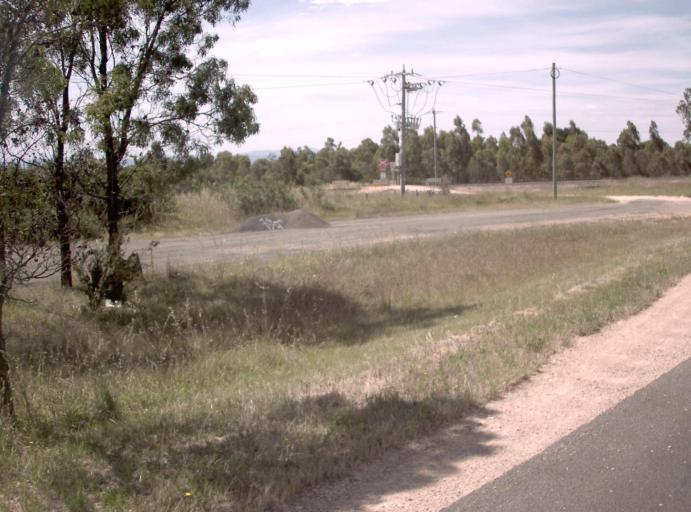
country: AU
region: Victoria
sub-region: Wellington
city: Sale
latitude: -37.9576
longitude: 147.0971
